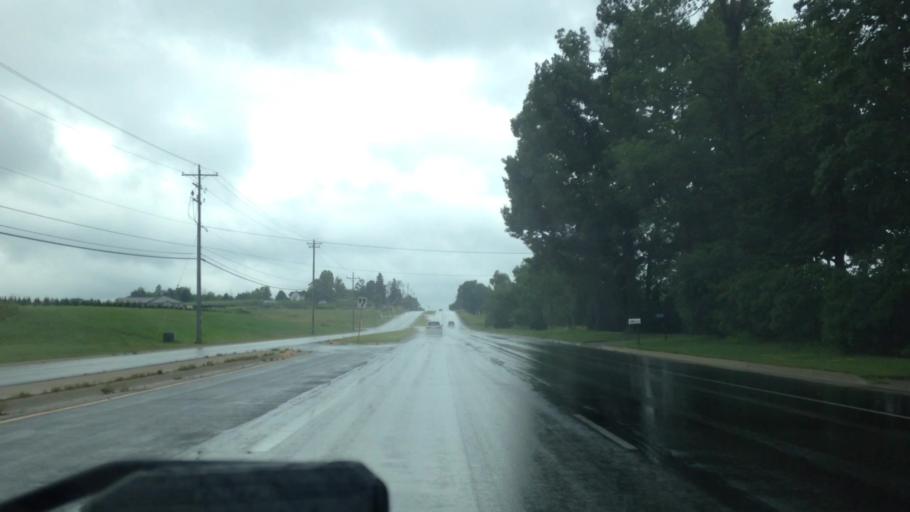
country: US
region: Wisconsin
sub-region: Waukesha County
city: Lannon
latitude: 43.1924
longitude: -88.1690
